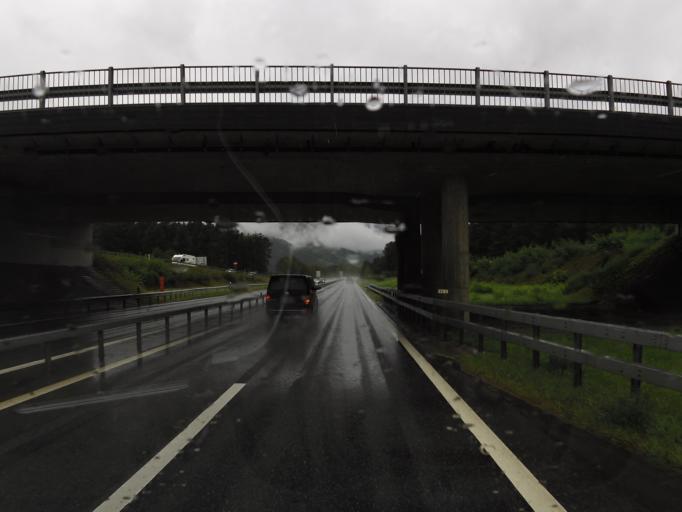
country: CH
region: Grisons
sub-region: Hinterrhein District
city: Thusis
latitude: 46.7140
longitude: 9.4457
